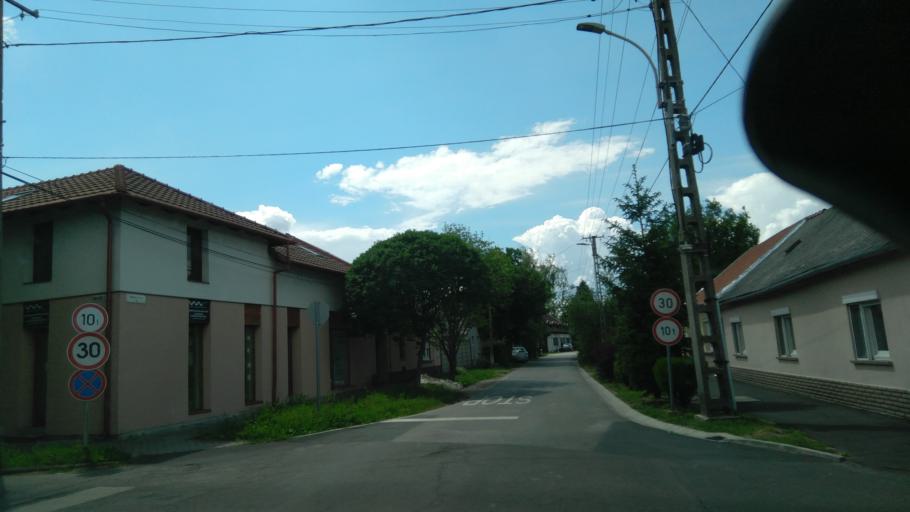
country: HU
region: Bekes
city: Gyula
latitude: 46.6468
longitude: 21.2621
